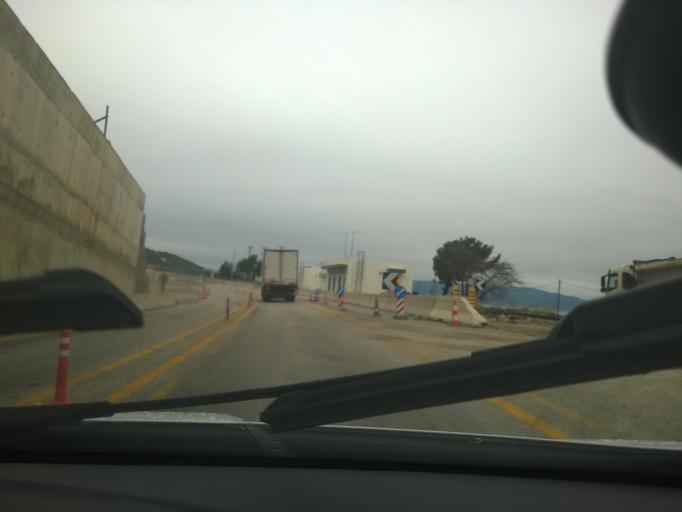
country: GR
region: West Greece
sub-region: Nomos Achaias
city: Kamarai
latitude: 38.3243
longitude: 21.9133
